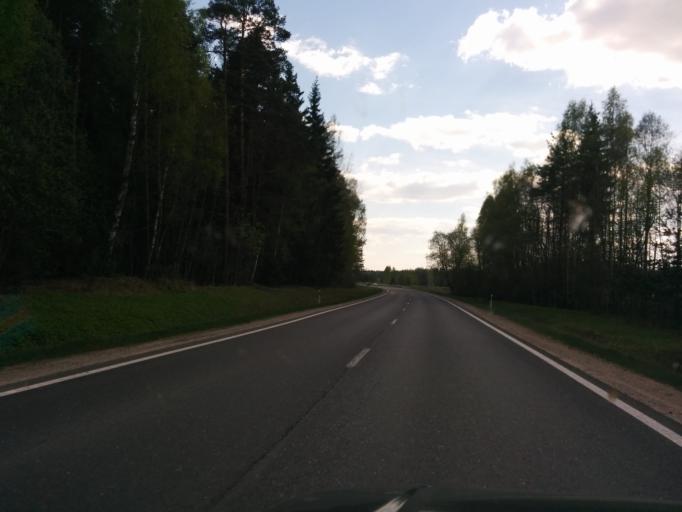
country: LV
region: Pargaujas
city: Stalbe
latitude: 57.3287
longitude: 24.9224
